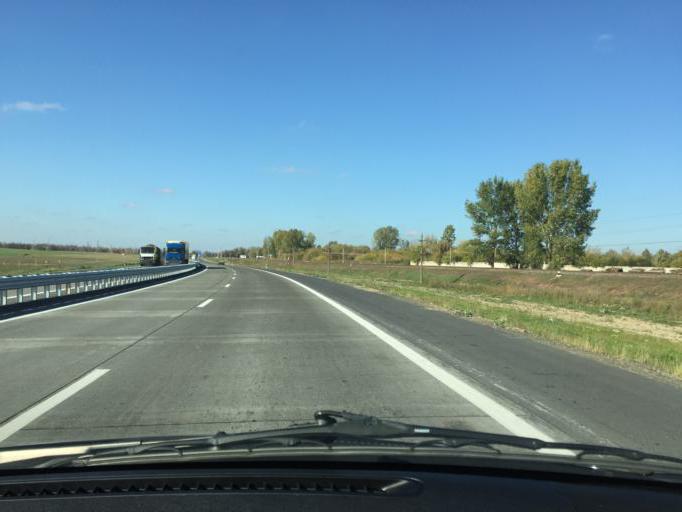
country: BY
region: Minsk
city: Slutsk
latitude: 52.9982
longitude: 27.5052
